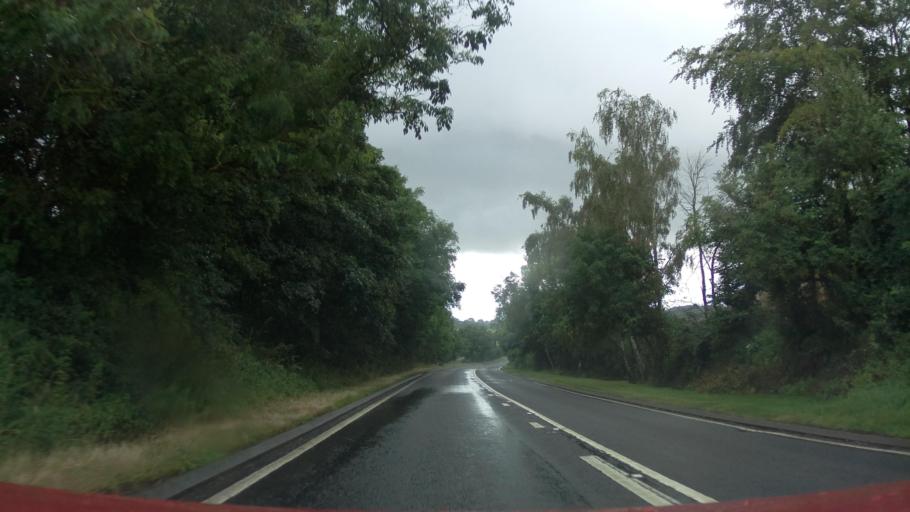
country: GB
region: England
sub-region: Oxfordshire
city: Claydon
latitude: 52.1441
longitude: -1.3591
